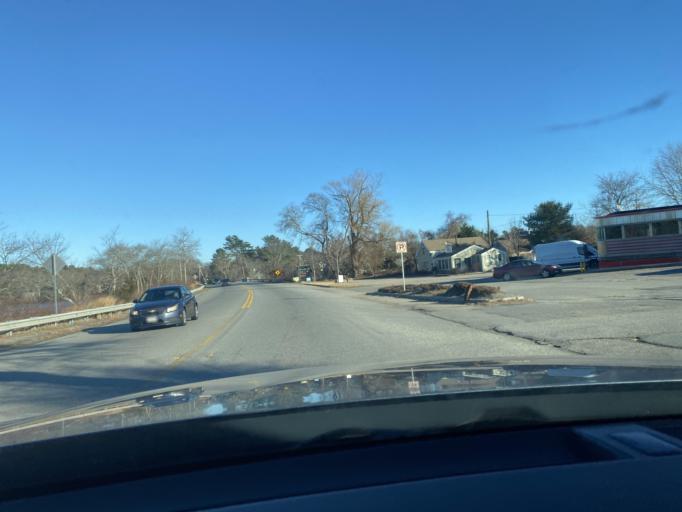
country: US
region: Massachusetts
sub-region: Plymouth County
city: Wareham Center
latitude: 41.7672
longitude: -70.7247
